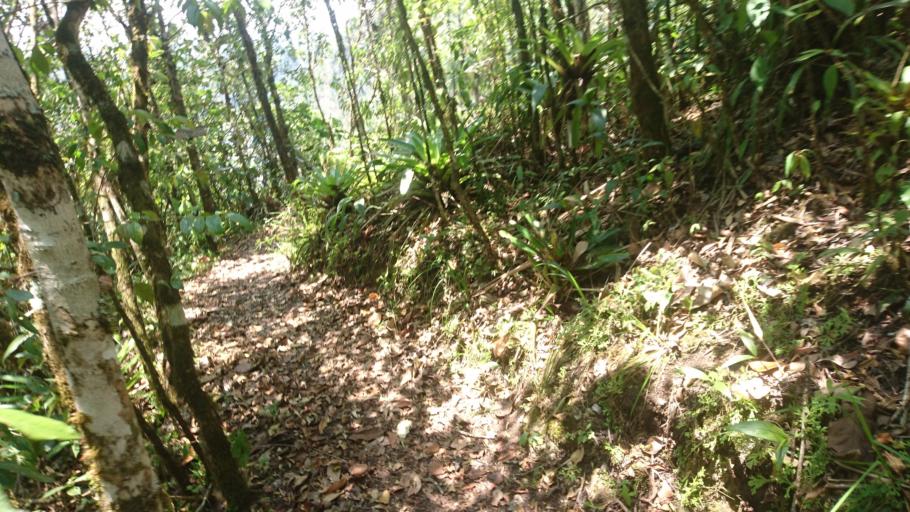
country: GT
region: Huehuetenango
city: Union
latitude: 16.1092
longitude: -91.6723
